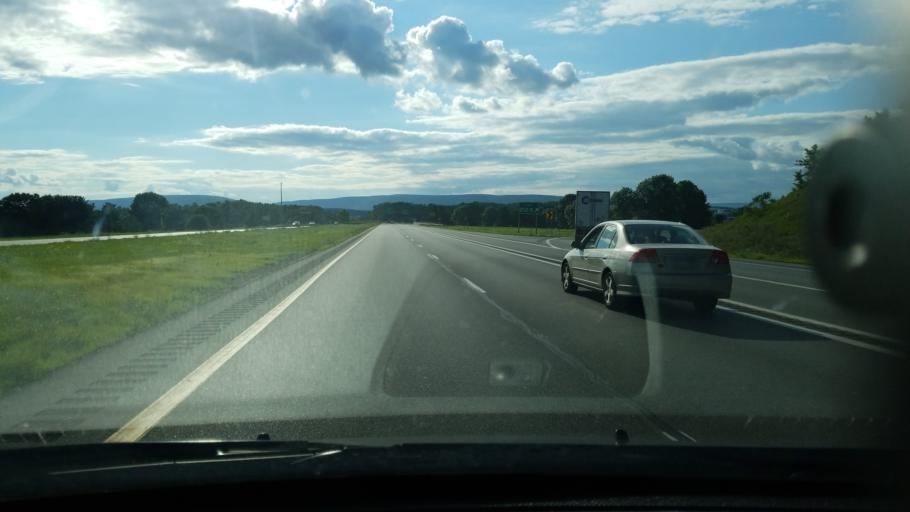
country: US
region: Pennsylvania
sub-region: Union County
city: New Columbia
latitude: 41.0487
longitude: -76.8357
